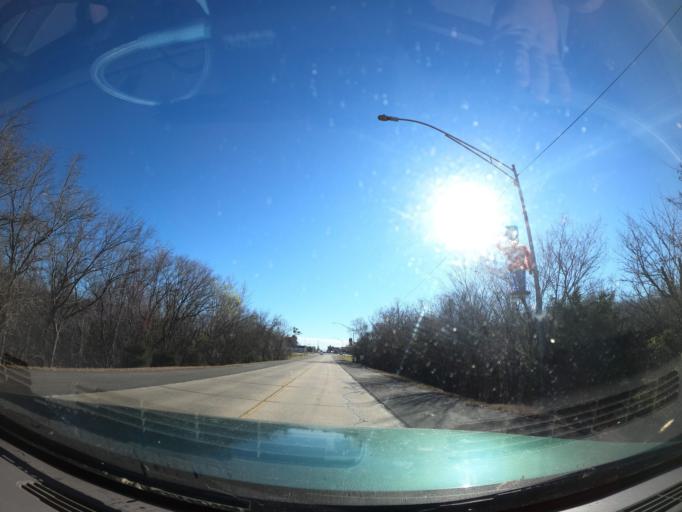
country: US
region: Oklahoma
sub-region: McIntosh County
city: Eufaula
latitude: 35.2922
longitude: -95.5824
